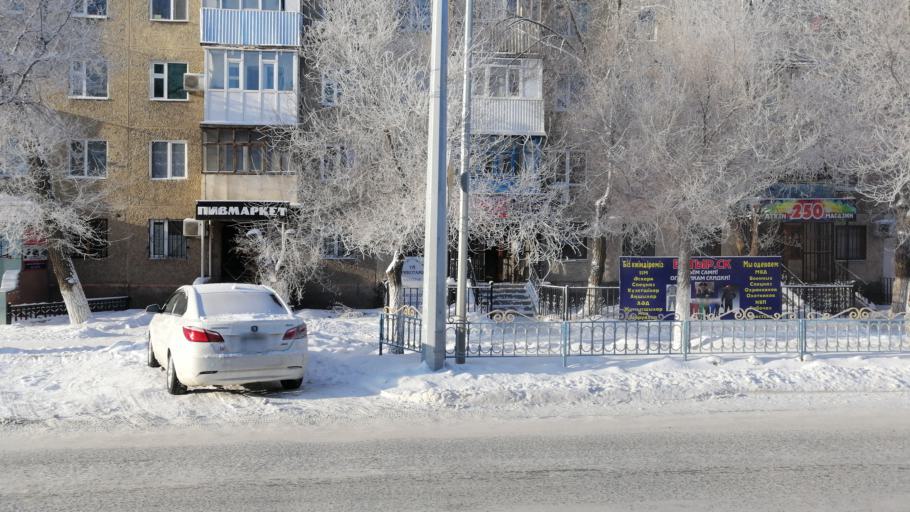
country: KZ
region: Aqtoebe
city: Aqtobe
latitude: 50.3060
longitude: 57.1505
